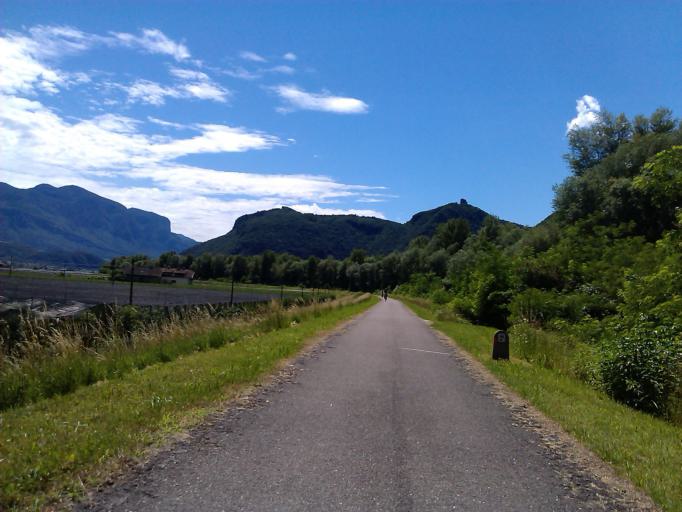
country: IT
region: Trentino-Alto Adige
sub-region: Bolzano
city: Vadena
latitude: 46.3966
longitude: 11.3000
